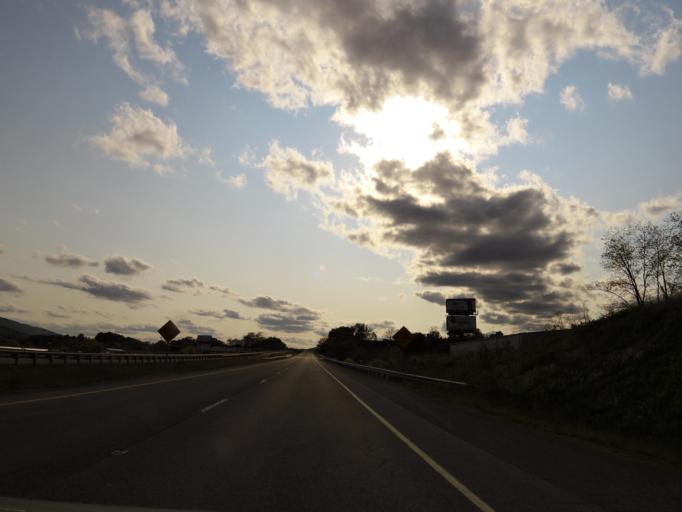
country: US
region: Virginia
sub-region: Tazewell County
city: Bluefield
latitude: 37.2353
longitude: -81.3024
